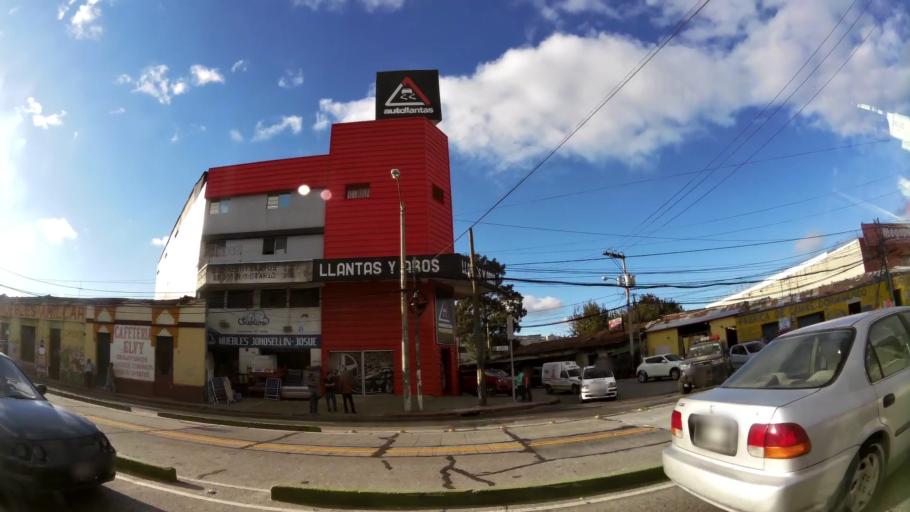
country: GT
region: Guatemala
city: Guatemala City
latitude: 14.6231
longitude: -90.5237
